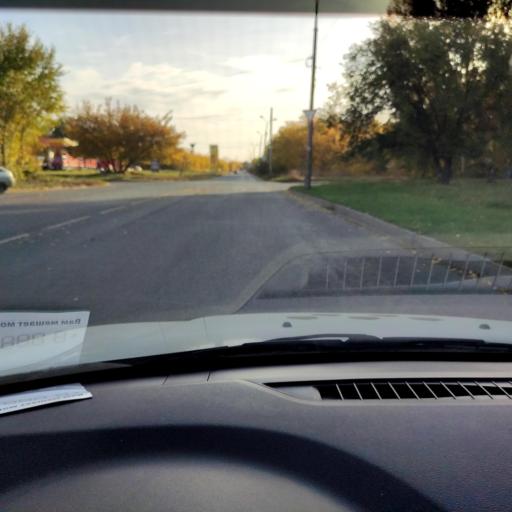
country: RU
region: Samara
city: Tol'yatti
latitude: 53.5556
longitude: 49.3084
